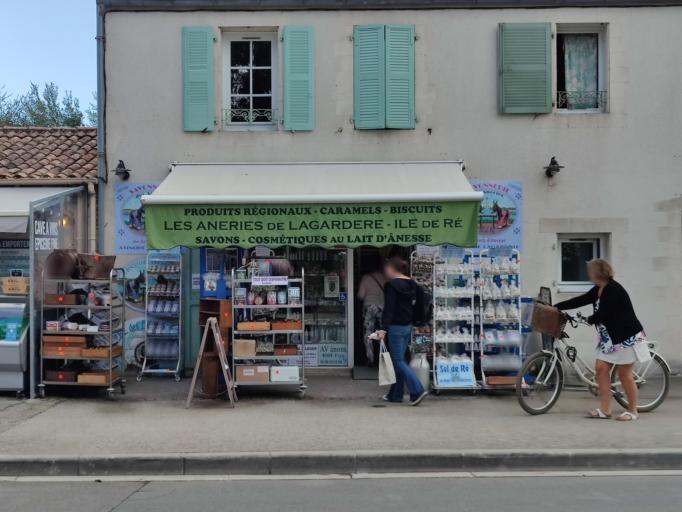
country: FR
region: Poitou-Charentes
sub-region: Departement de la Charente-Maritime
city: Saint-Martin-de-Re
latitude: 46.2056
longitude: -1.3639
